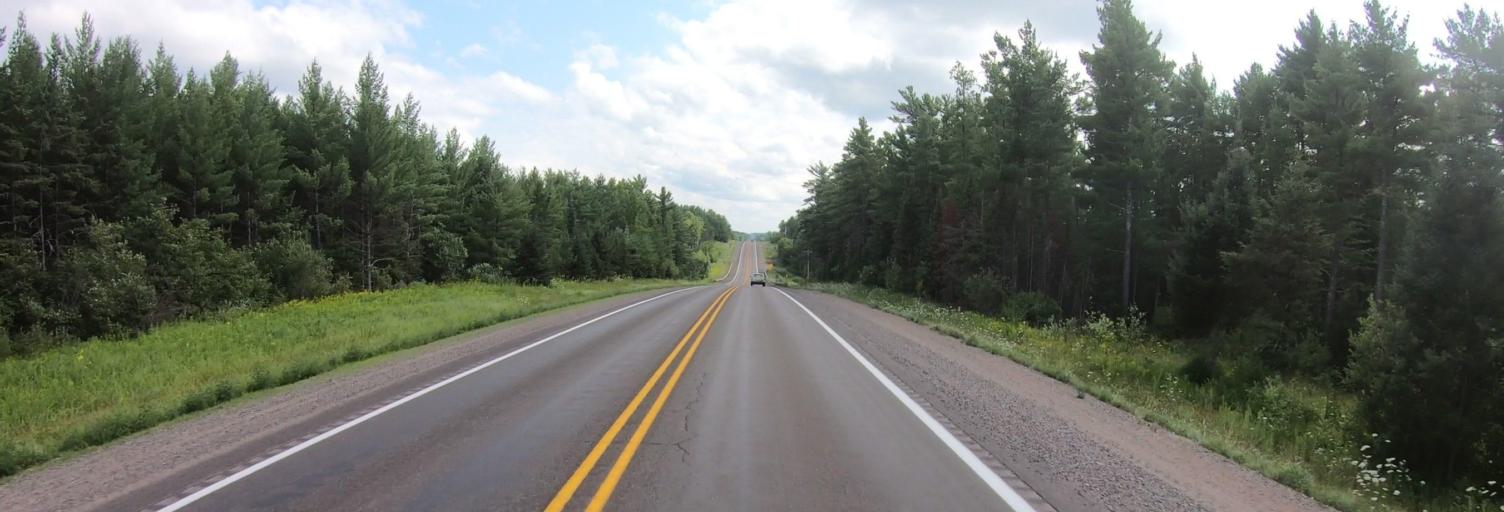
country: US
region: Michigan
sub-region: Ontonagon County
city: Ontonagon
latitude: 46.5583
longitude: -89.1786
